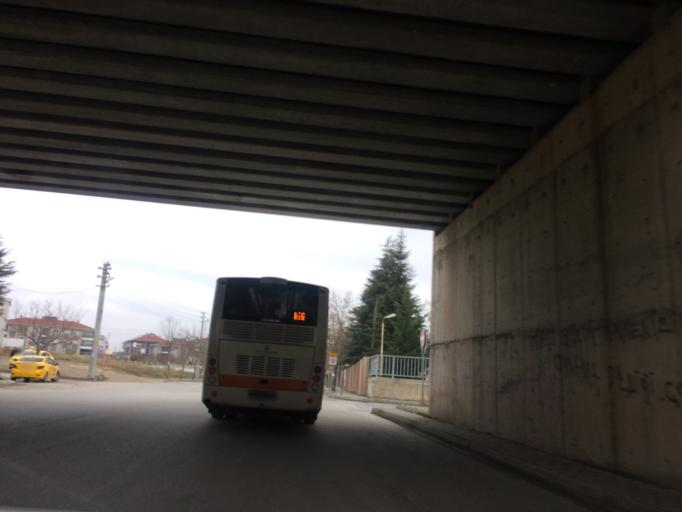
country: TR
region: Eskisehir
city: Eskisehir
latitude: 39.7790
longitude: 30.4841
